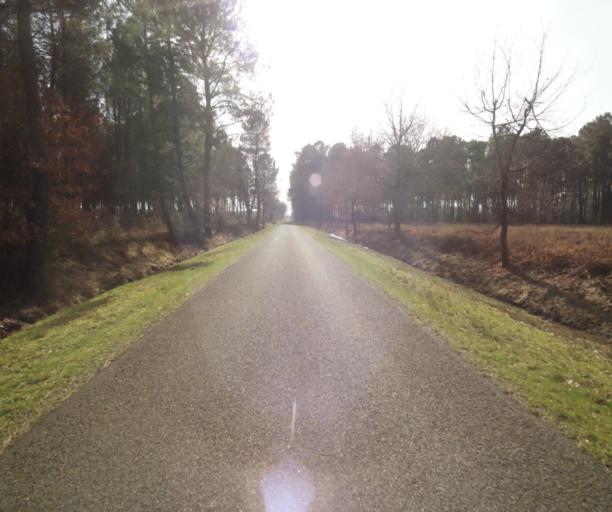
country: FR
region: Aquitaine
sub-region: Departement des Landes
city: Roquefort
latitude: 44.1595
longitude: -0.1679
